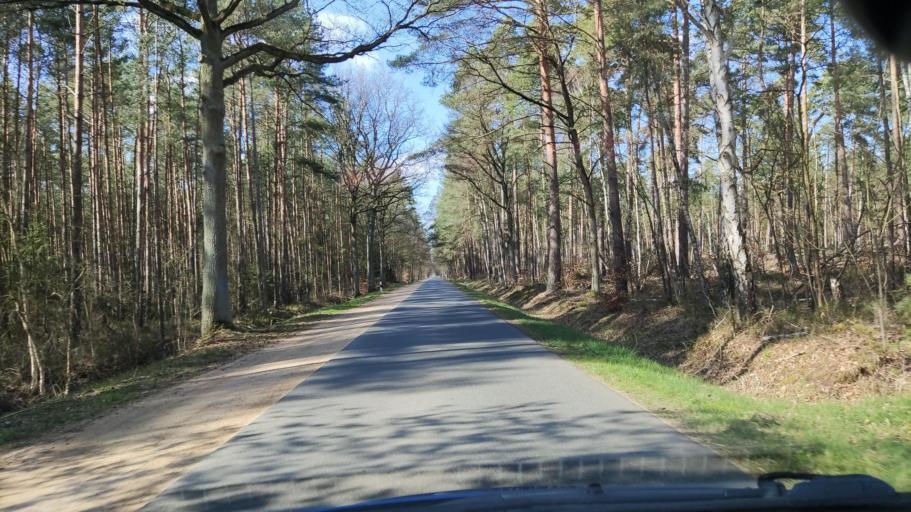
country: DE
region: Lower Saxony
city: Langendorf
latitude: 53.0370
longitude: 11.2545
